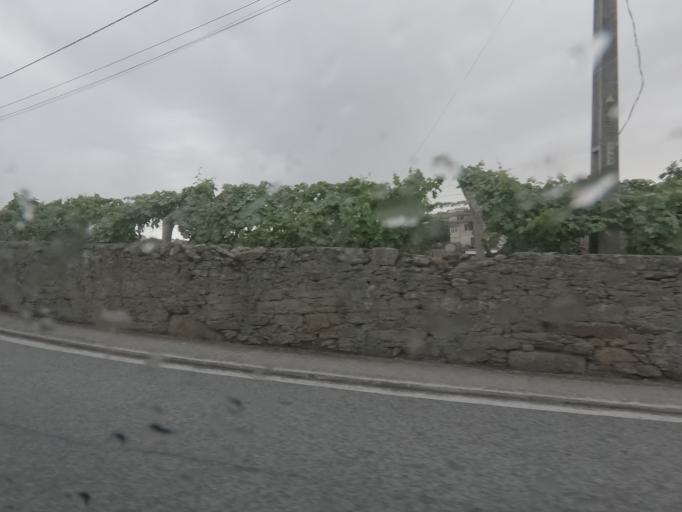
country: PT
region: Viseu
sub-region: Armamar
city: Armamar
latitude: 41.1220
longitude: -7.7312
